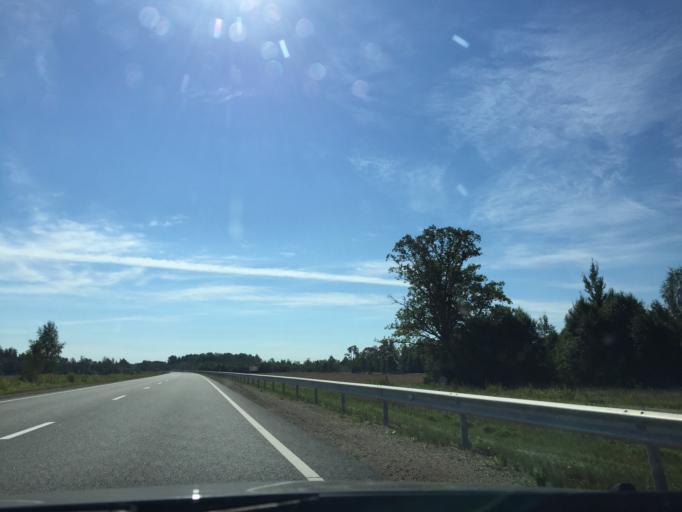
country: LV
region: Skriveri
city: Skriveri
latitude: 56.7468
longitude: 25.1246
